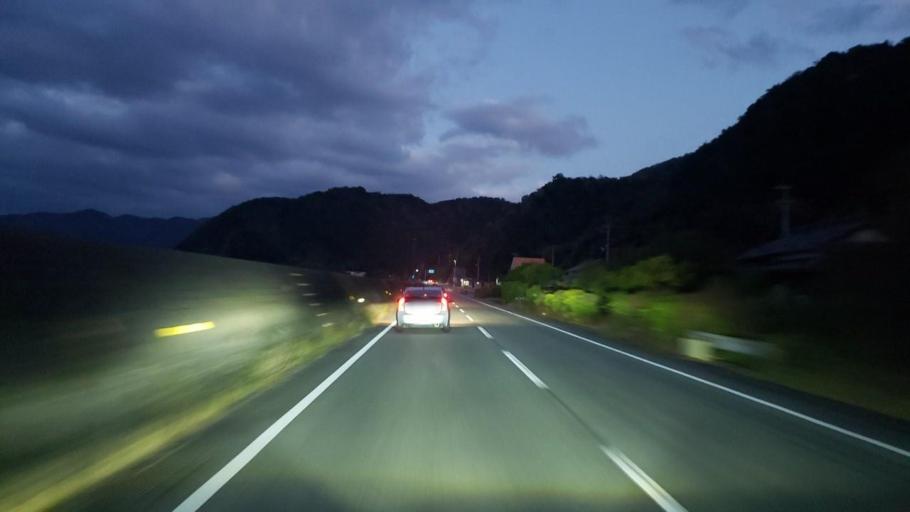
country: JP
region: Tokushima
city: Ishii
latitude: 34.2066
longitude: 134.4452
